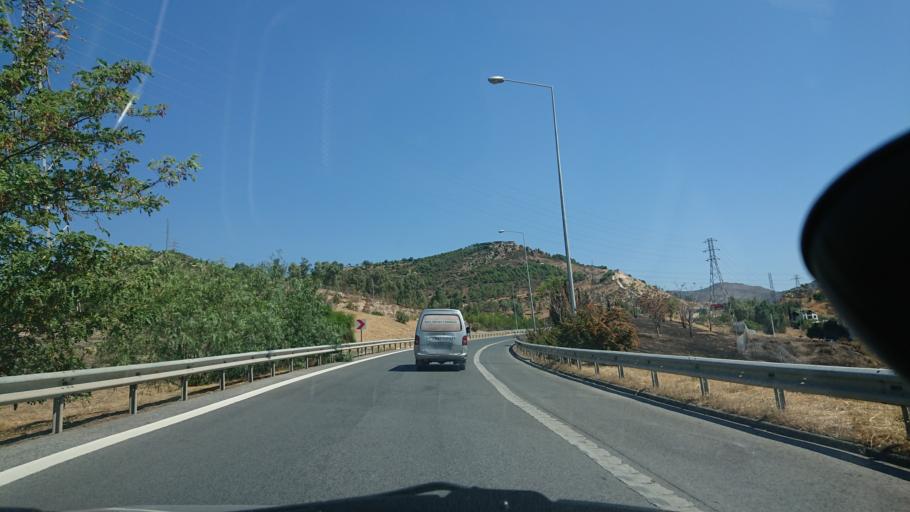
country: TR
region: Izmir
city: Karsiyaka
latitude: 38.4856
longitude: 27.1161
